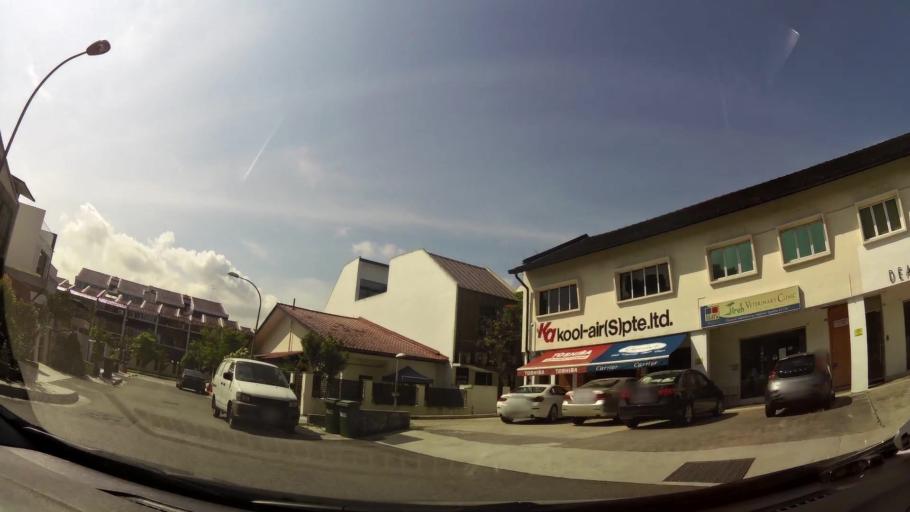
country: SG
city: Singapore
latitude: 1.3584
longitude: 103.8277
